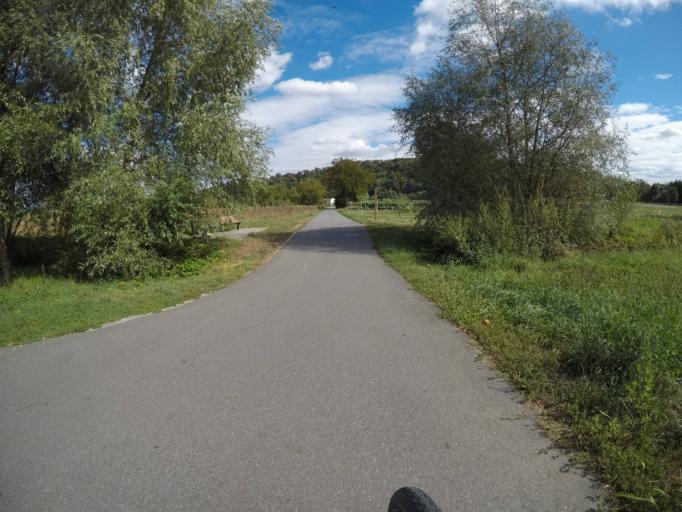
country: DE
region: Baden-Wuerttemberg
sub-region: Karlsruhe Region
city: Hassmersheim
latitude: 49.2952
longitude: 9.1418
